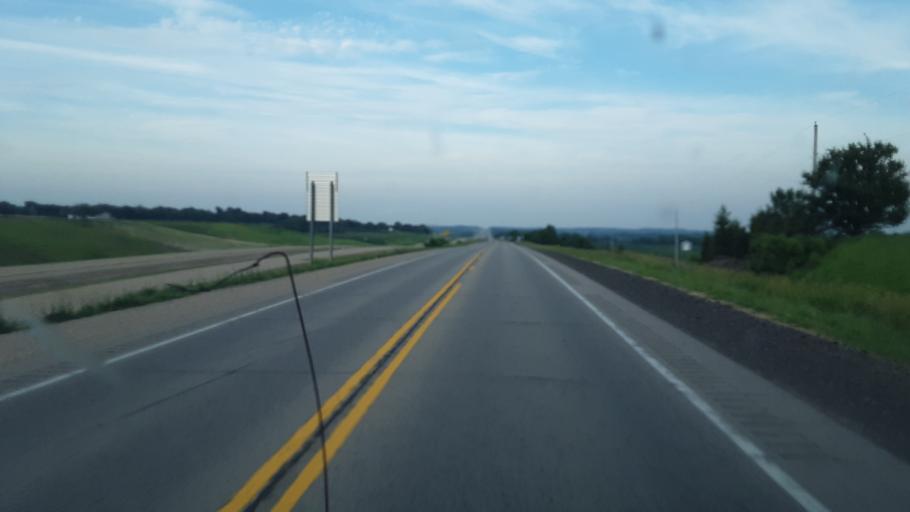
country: US
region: Iowa
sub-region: Tama County
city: Tama
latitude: 41.9638
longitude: -92.5210
